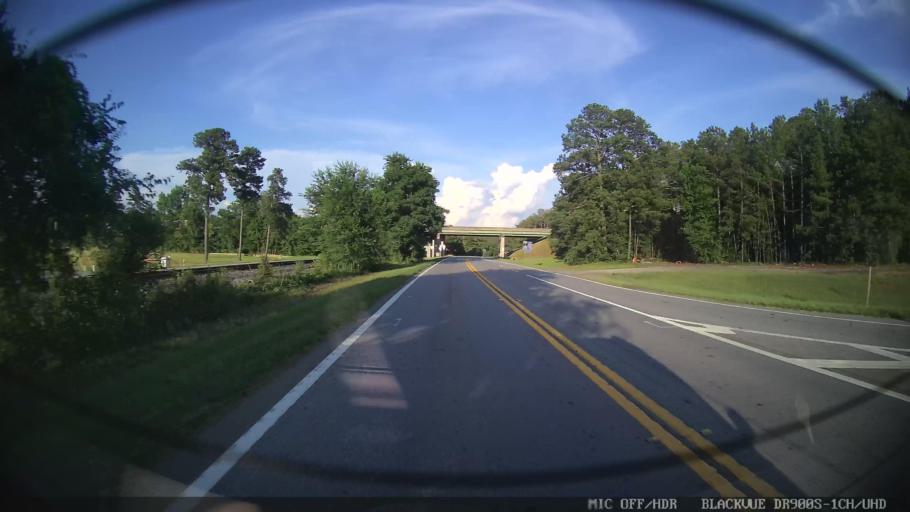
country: US
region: Georgia
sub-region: Monroe County
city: Forsyth
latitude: 32.9497
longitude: -83.8253
